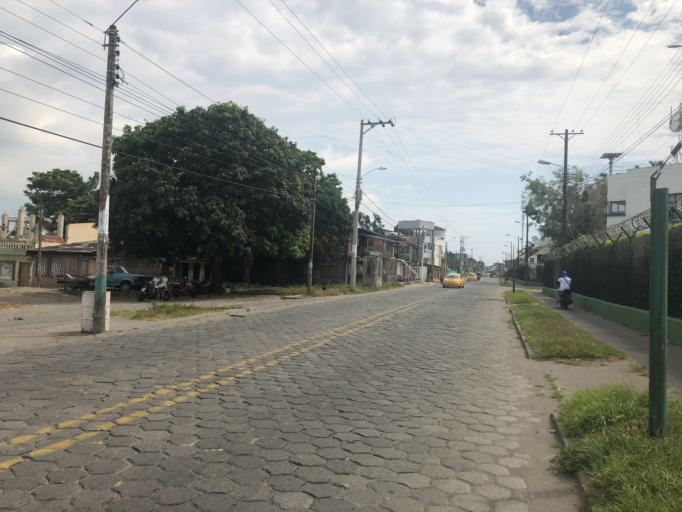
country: CO
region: Narino
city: Tumaco
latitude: 1.8203
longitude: -78.7469
